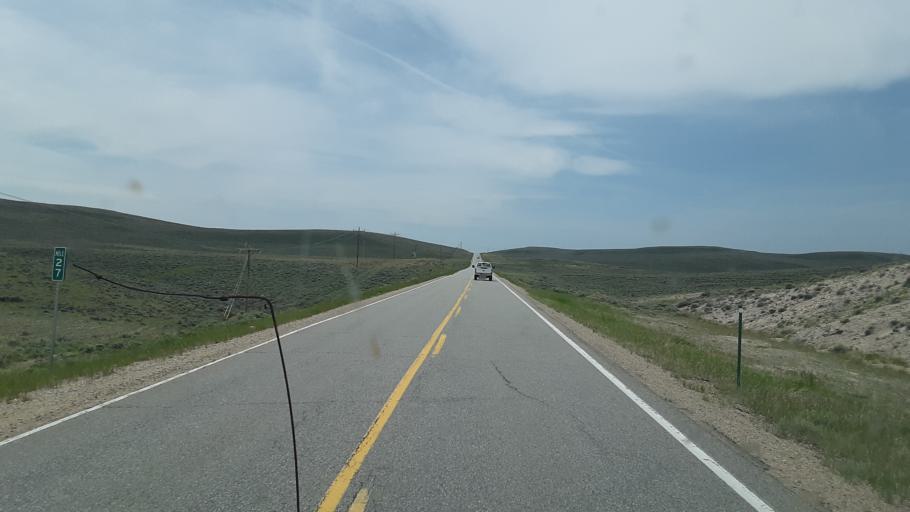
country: US
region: Colorado
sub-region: Jackson County
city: Walden
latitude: 40.6697
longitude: -106.3846
